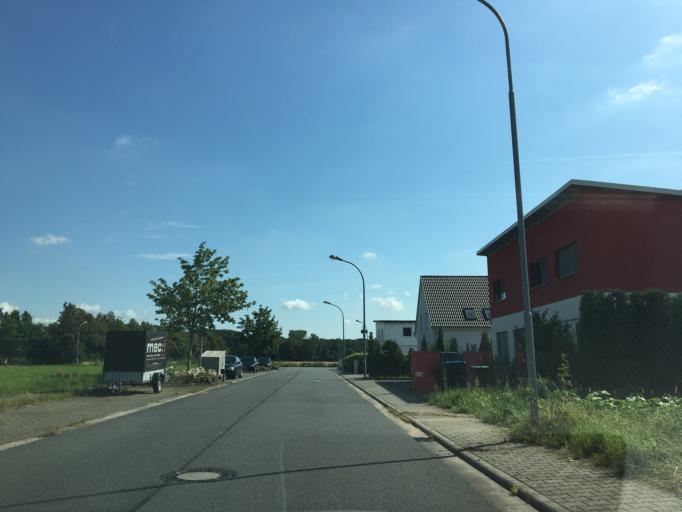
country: DE
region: Hesse
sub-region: Regierungsbezirk Darmstadt
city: Egelsbach
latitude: 49.9590
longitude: 8.6667
